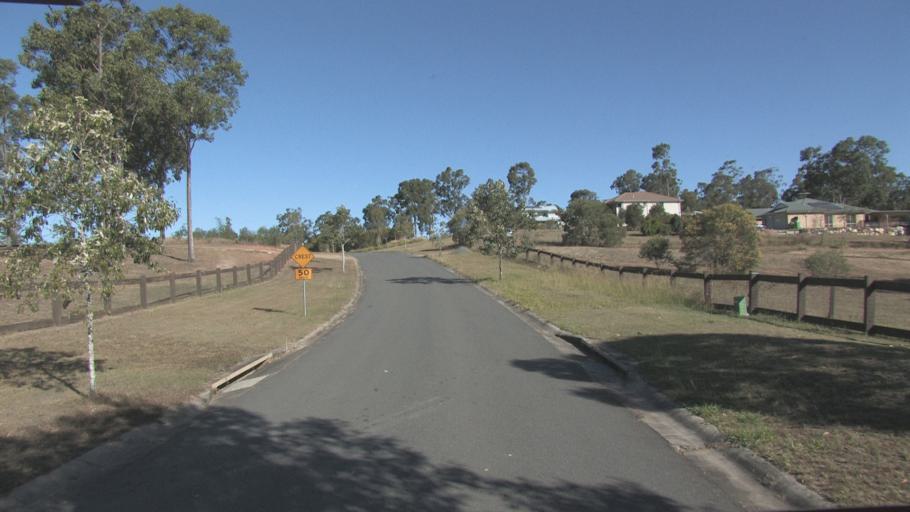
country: AU
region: Queensland
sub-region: Ipswich
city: Springfield Lakes
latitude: -27.7179
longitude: 152.9204
